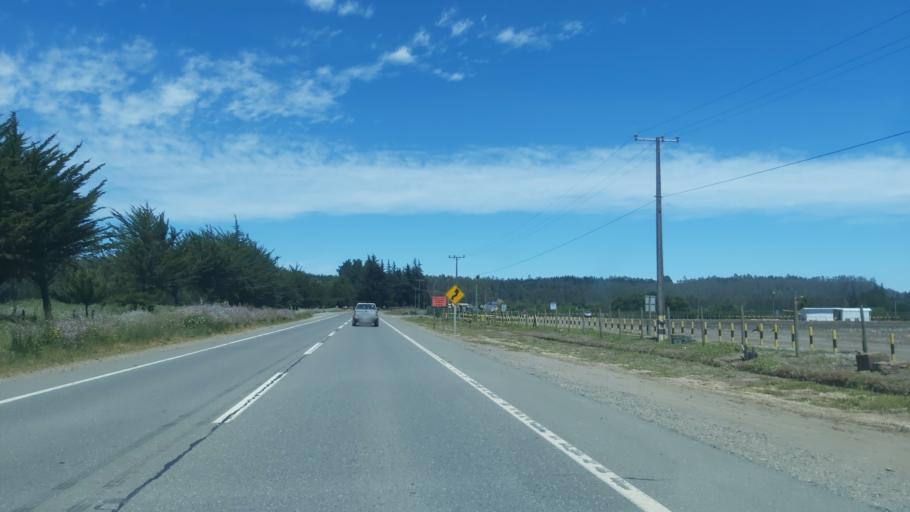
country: CL
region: Maule
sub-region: Provincia de Talca
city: Constitucion
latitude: -35.3097
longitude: -72.3809
